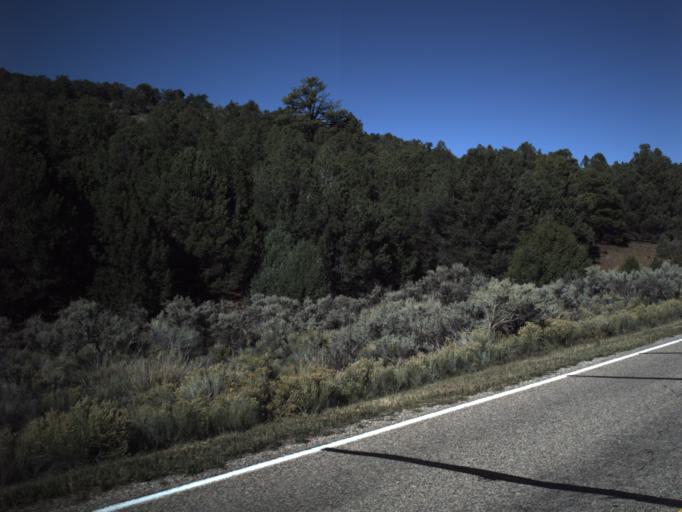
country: US
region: Utah
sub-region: Garfield County
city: Panguitch
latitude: 37.7659
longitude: -112.4899
